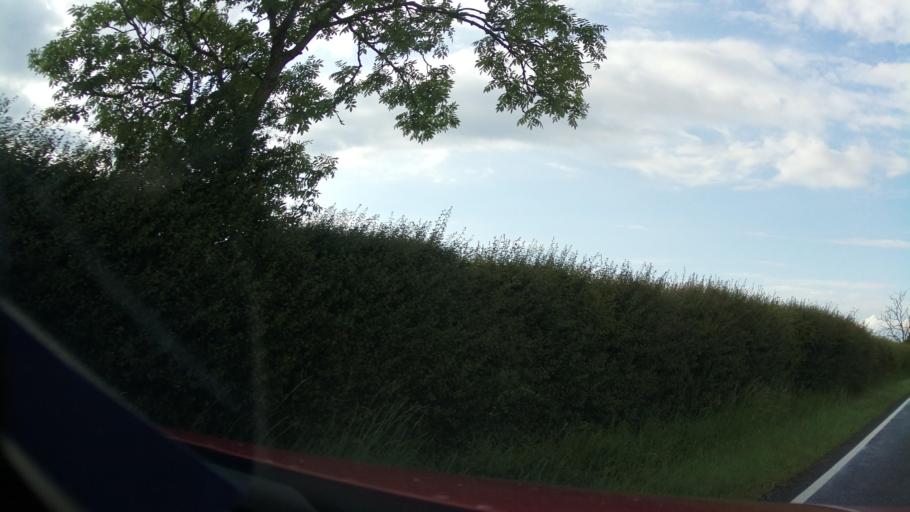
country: GB
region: England
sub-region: Lincolnshire
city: Great Gonerby
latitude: 53.0041
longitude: -0.6669
